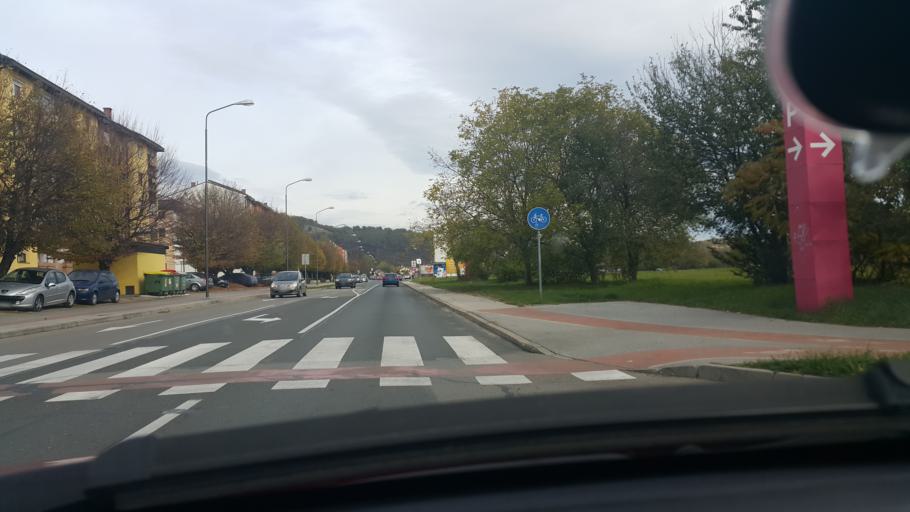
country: SI
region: Maribor
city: Maribor
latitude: 46.5490
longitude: 15.6756
